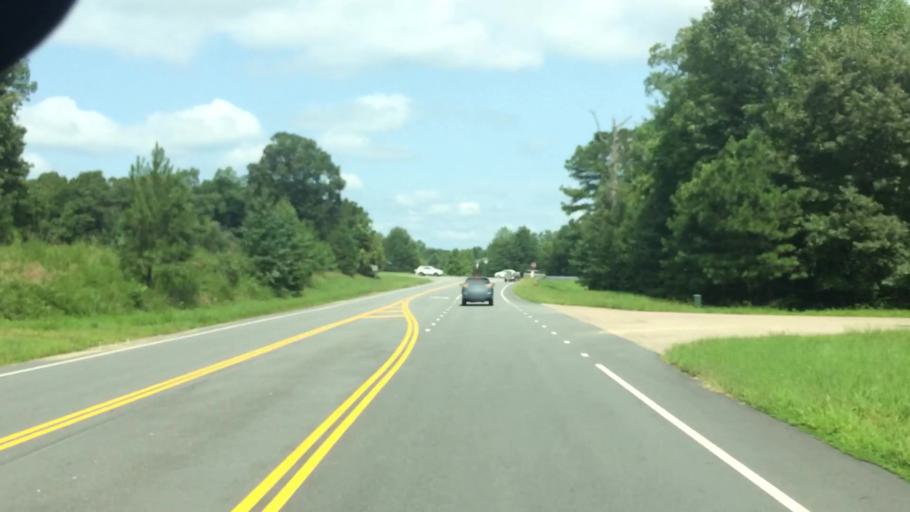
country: US
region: Virginia
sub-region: James City County
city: Williamsburg
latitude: 37.2618
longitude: -76.7884
